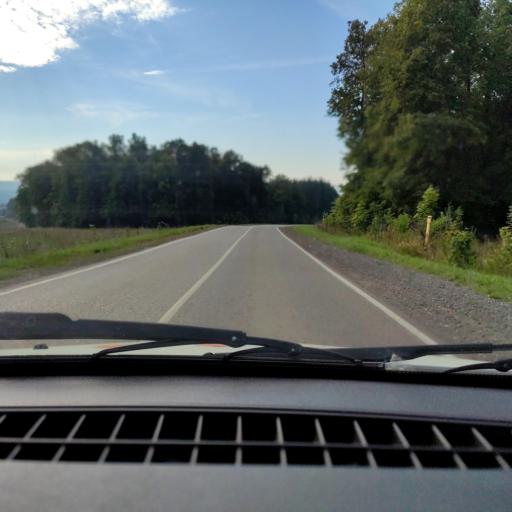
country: RU
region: Bashkortostan
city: Avdon
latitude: 54.6255
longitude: 55.6274
